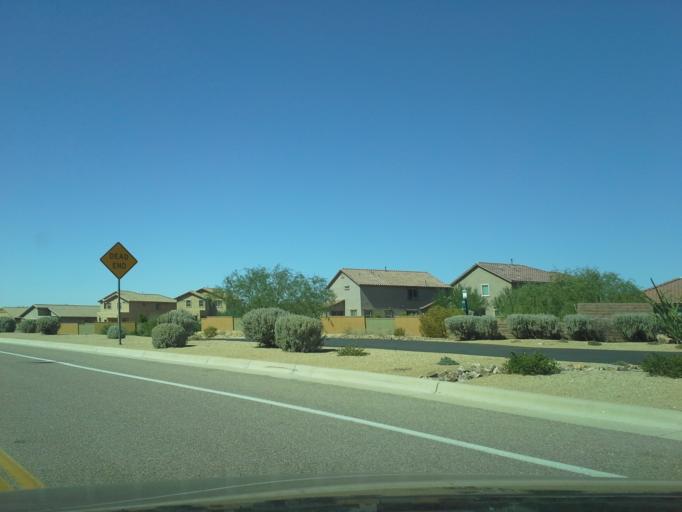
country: US
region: Arizona
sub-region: Pima County
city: Marana
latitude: 32.4650
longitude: -111.2131
